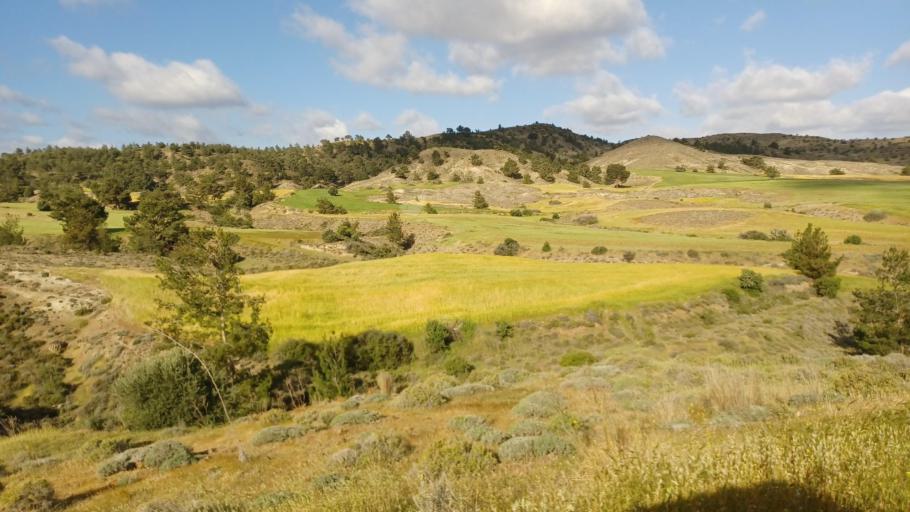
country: CY
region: Lefkosia
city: Peristerona
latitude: 35.0679
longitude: 33.0471
